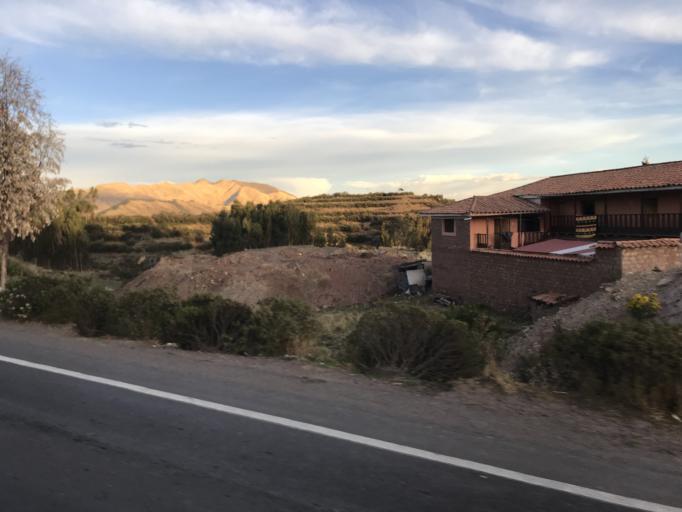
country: PE
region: Cusco
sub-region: Provincia de Cusco
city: Cusco
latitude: -13.4919
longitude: -71.9662
